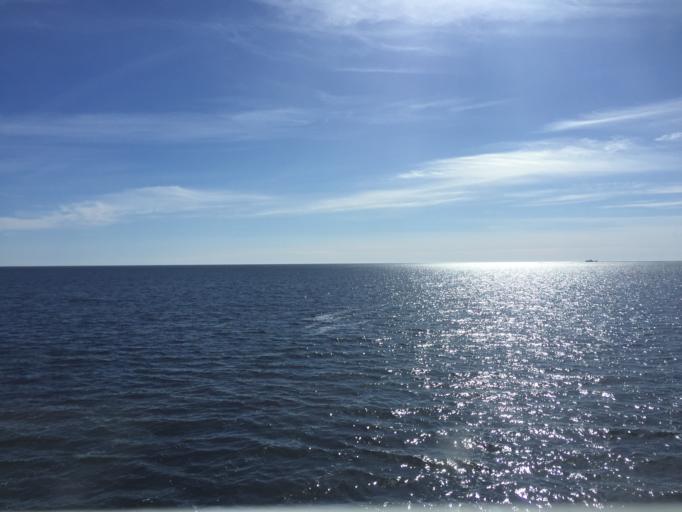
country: EE
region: Laeaene
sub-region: Haapsalu linn
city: Haapsalu
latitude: 58.5759
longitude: 23.4667
